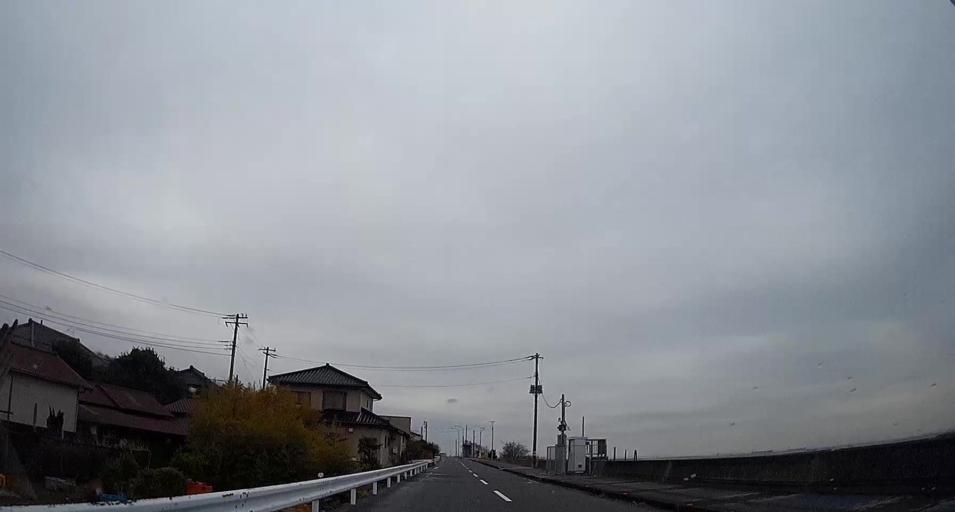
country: JP
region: Chiba
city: Kisarazu
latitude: 35.4360
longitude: 139.9136
